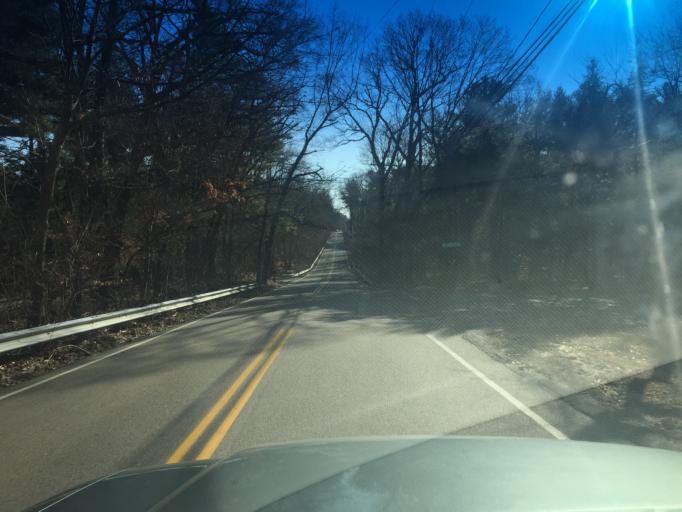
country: US
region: Massachusetts
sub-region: Norfolk County
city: Millis
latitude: 42.1905
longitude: -71.3758
